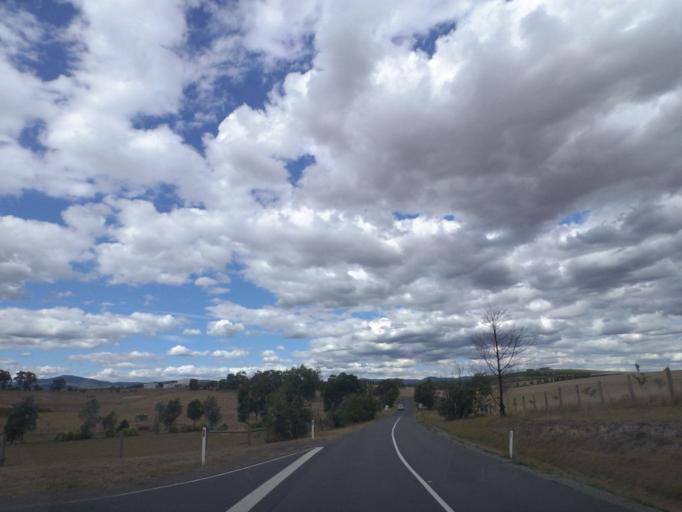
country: AU
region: Victoria
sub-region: Yarra Ranges
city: Yarra Glen
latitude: -37.6445
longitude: 145.4028
